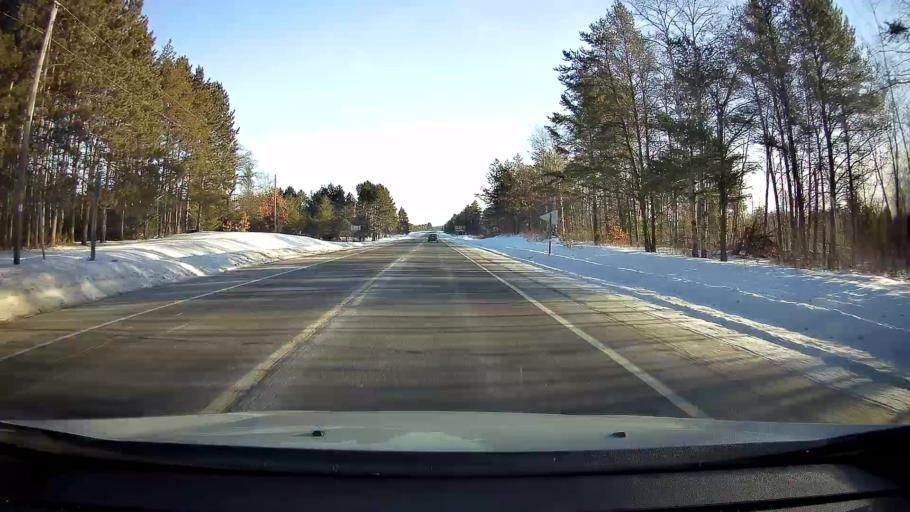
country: US
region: Wisconsin
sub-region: Washburn County
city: Spooner
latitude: 45.9119
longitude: -91.7567
